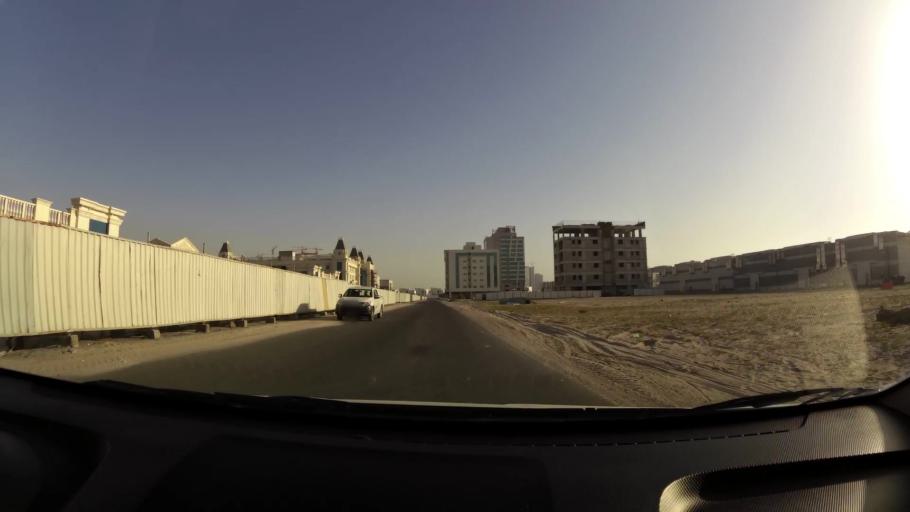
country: AE
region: Ajman
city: Ajman
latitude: 25.4044
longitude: 55.4854
